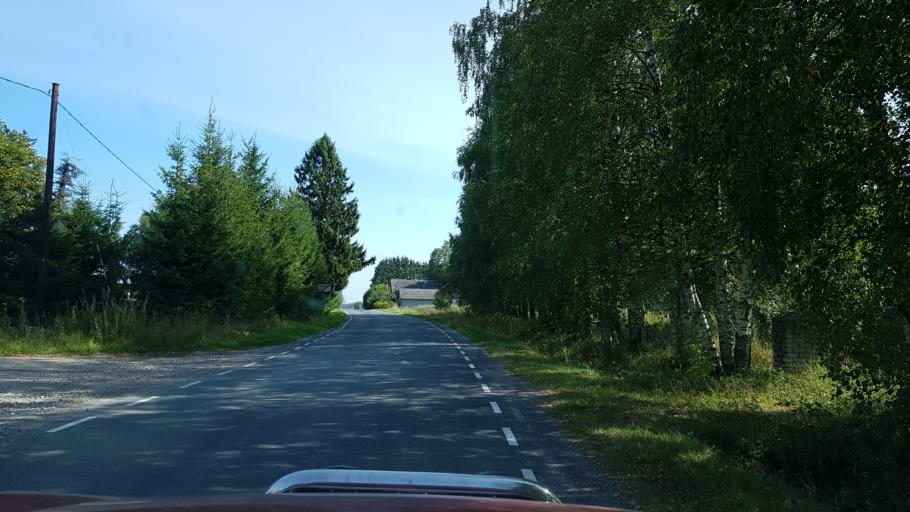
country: EE
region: Viljandimaa
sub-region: Suure-Jaani vald
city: Suure-Jaani
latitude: 58.4876
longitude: 25.5224
